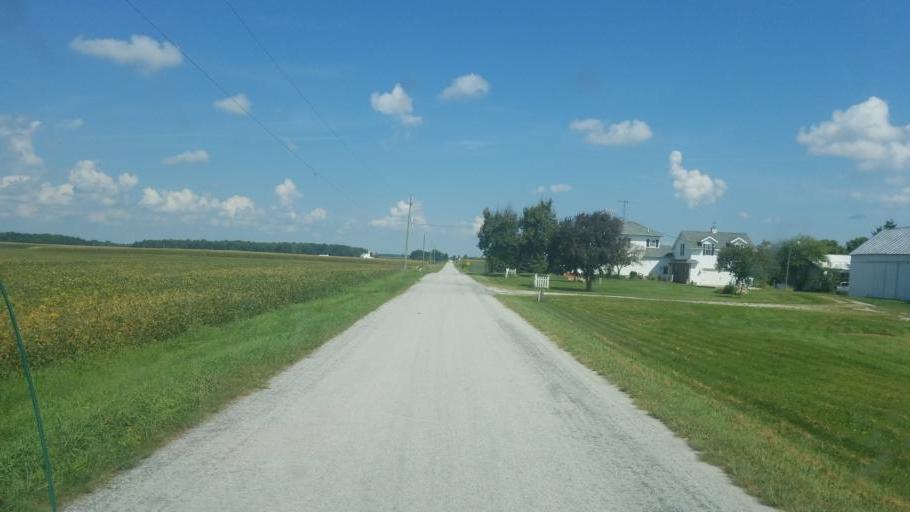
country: US
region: Ohio
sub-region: Hardin County
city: Kenton
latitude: 40.6768
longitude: -83.4957
